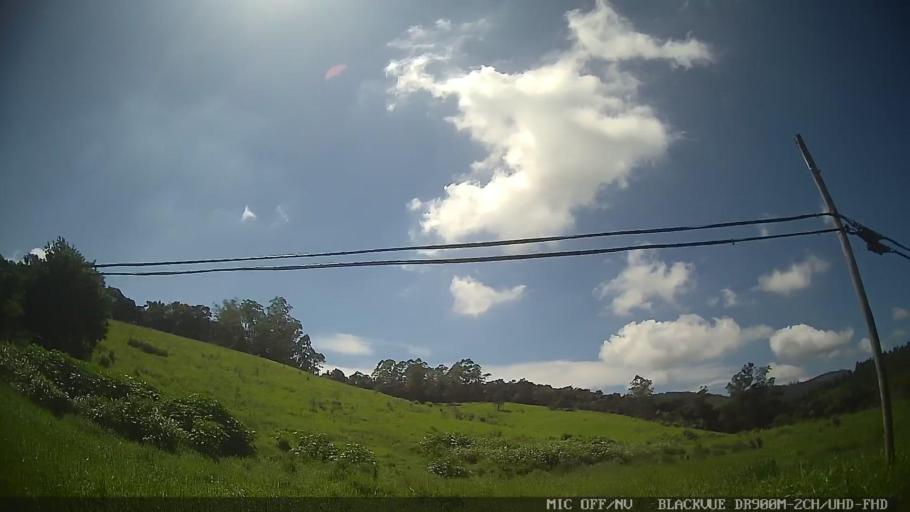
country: BR
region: Sao Paulo
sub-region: Mogi das Cruzes
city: Mogi das Cruzes
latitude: -23.6799
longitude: -46.2131
